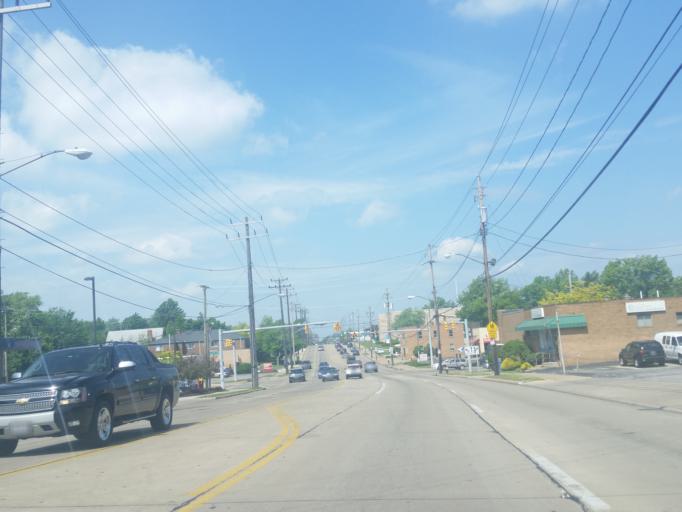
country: US
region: Ohio
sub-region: Cuyahoga County
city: South Euclid
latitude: 41.5208
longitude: -81.5260
